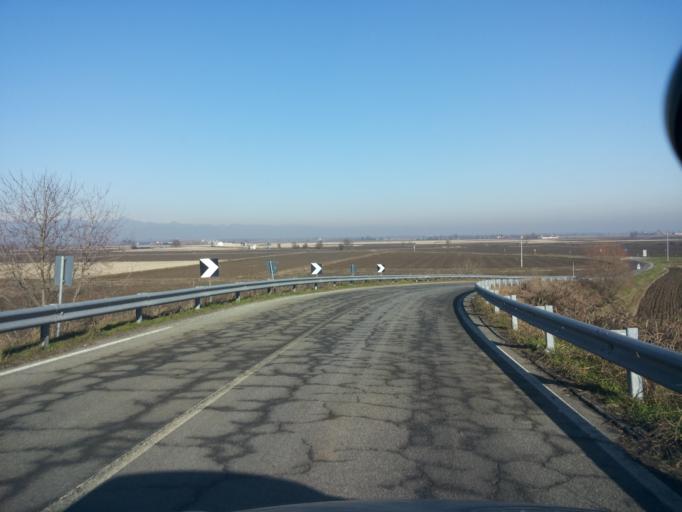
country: IT
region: Piedmont
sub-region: Provincia di Vercelli
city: San Germano Vercellese
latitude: 45.3552
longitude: 8.2433
